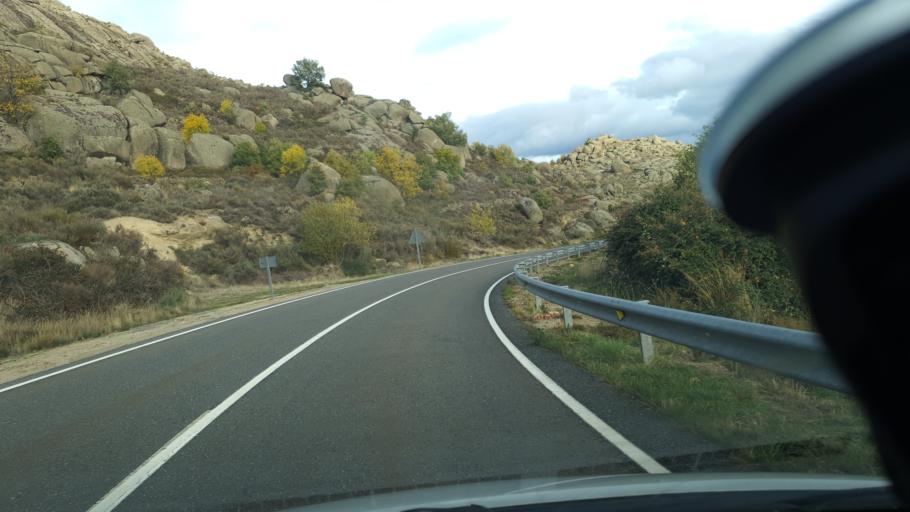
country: ES
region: Castille and Leon
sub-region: Provincia de Avila
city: Navalosa
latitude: 40.3959
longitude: -4.9207
